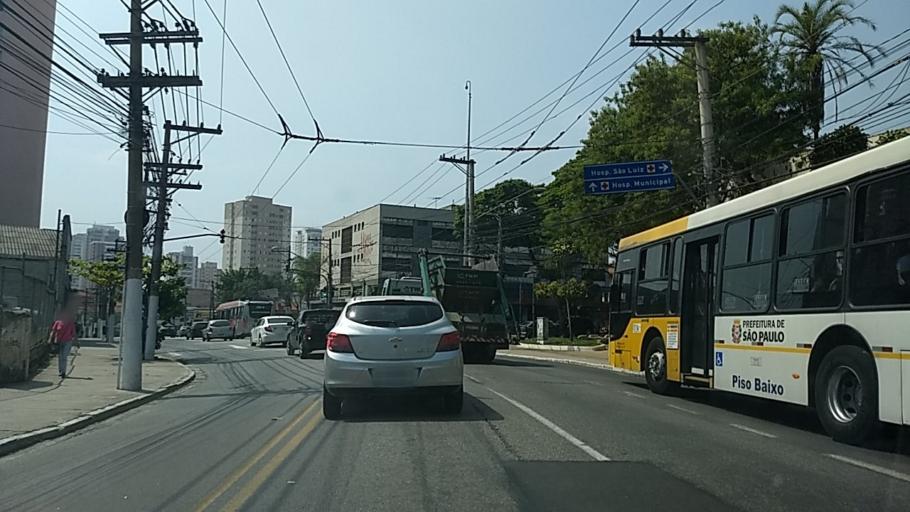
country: BR
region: Sao Paulo
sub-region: Sao Paulo
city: Sao Paulo
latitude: -23.5359
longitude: -46.5723
